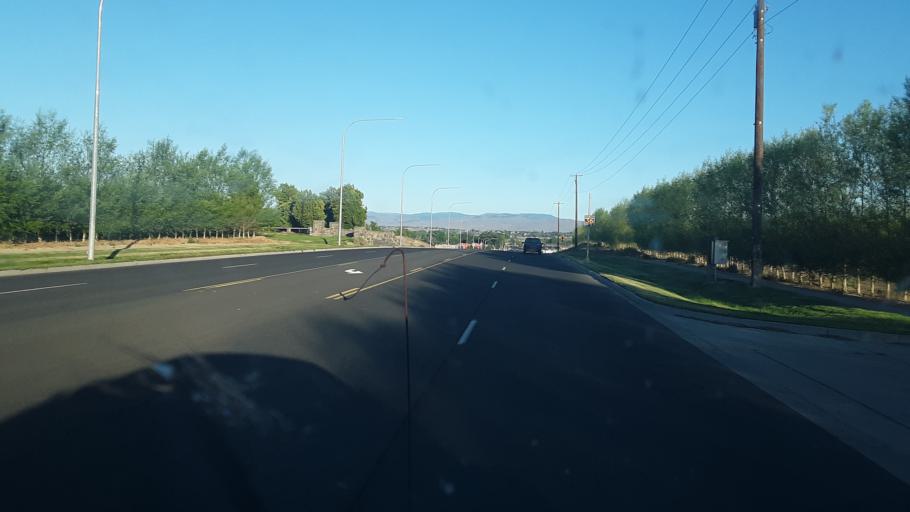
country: US
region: Washington
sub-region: Yakima County
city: West Valley
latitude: 46.5856
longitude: -120.5881
